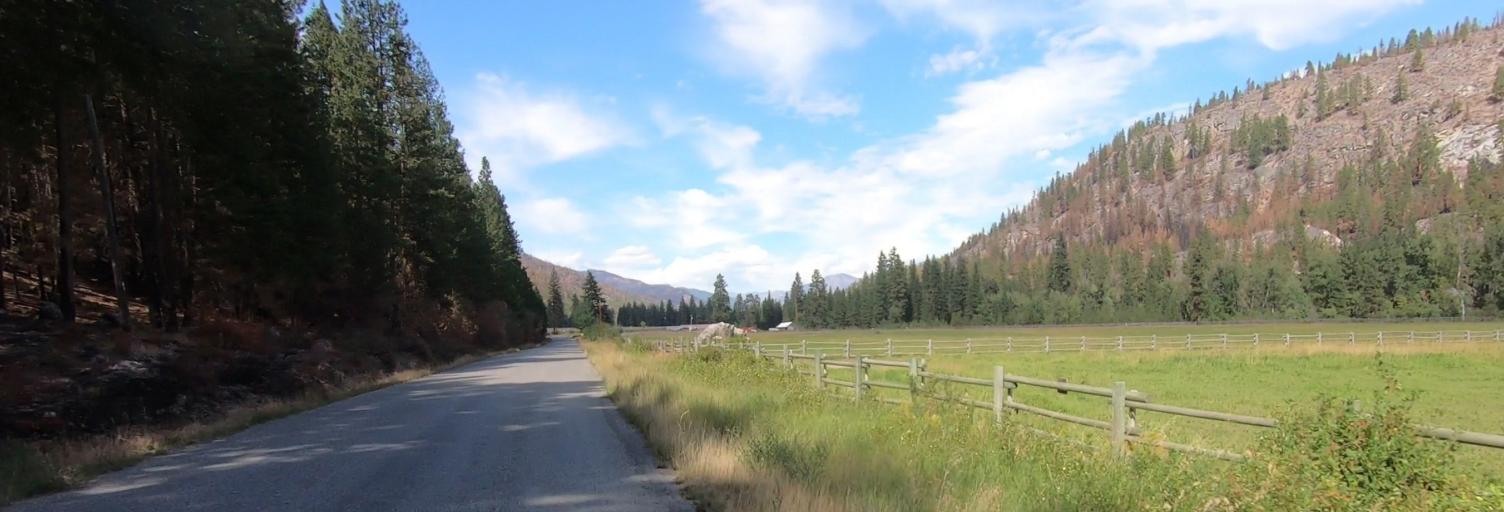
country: US
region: Washington
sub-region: Okanogan County
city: Okanogan
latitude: 48.5951
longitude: -120.1671
